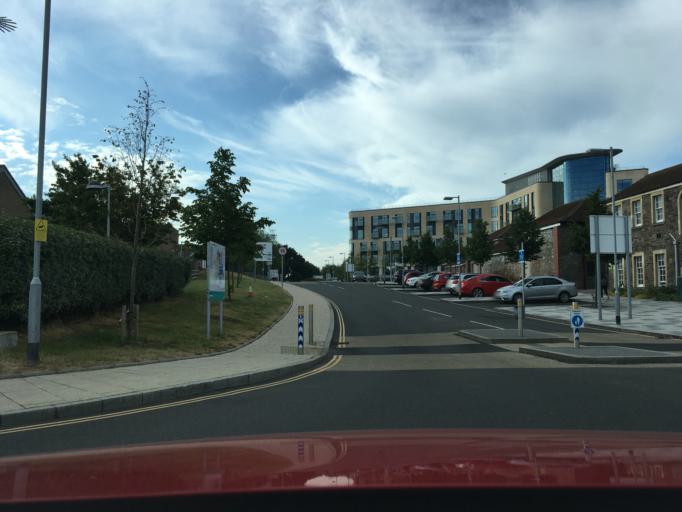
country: GB
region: England
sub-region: Bristol
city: Bristol
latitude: 51.4979
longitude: -2.5928
